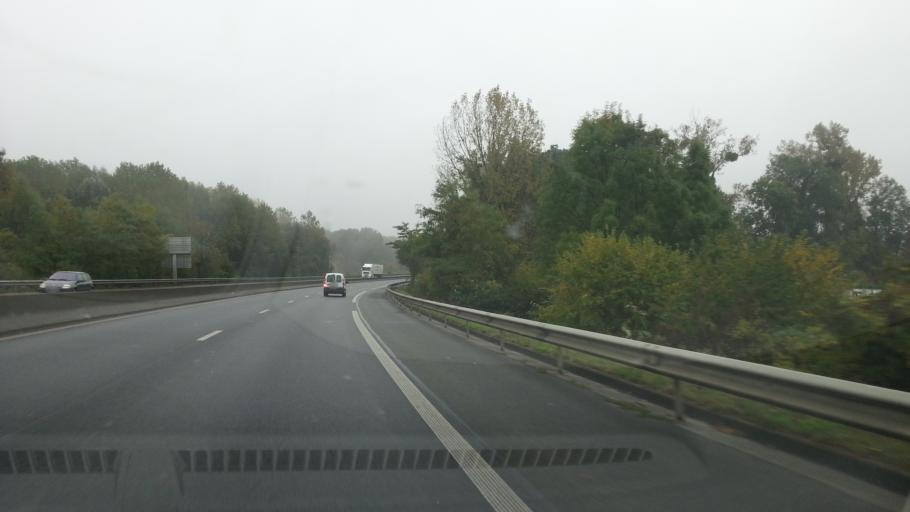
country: FR
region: Picardie
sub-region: Departement de l'Oise
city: Cauffry
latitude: 49.3102
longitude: 2.4510
